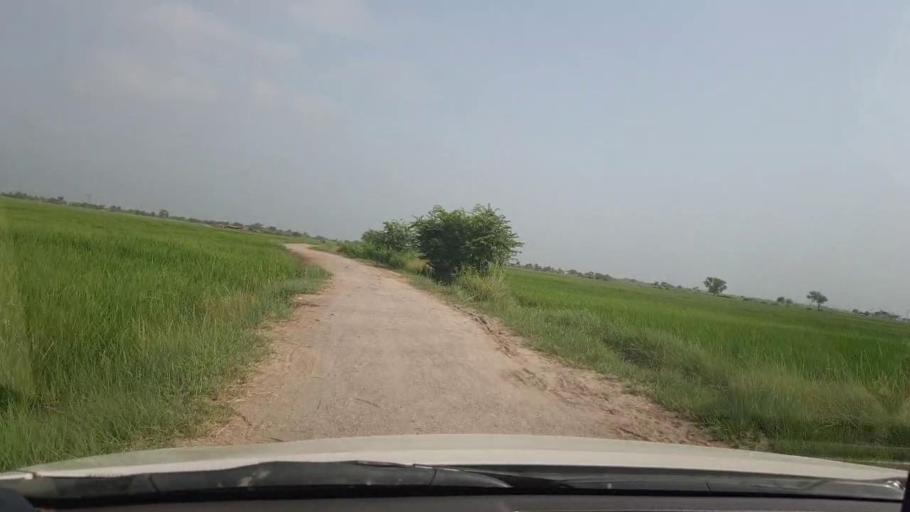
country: PK
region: Sindh
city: Shikarpur
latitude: 27.9851
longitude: 68.6093
